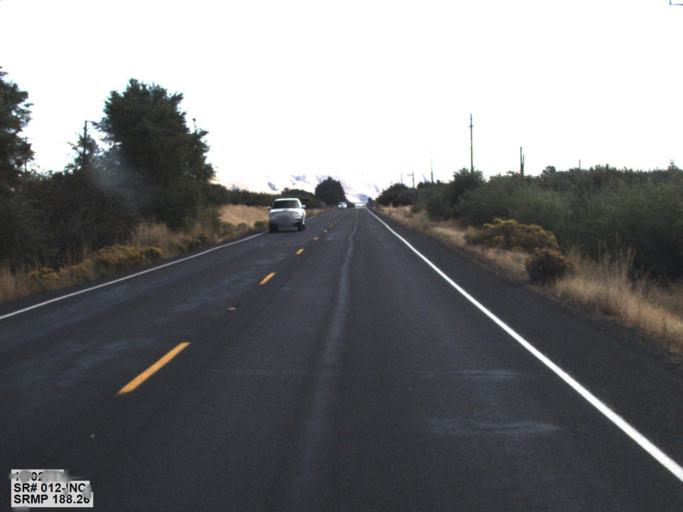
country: US
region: Washington
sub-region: Yakima County
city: Tieton
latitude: 46.7370
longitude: -120.7316
